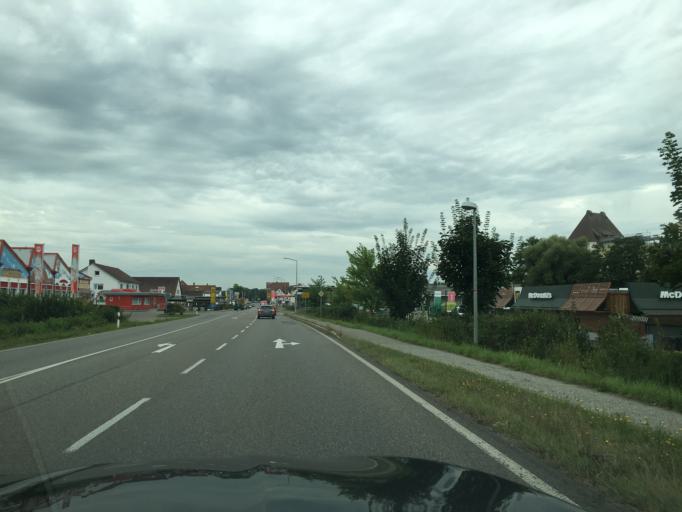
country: DE
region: Baden-Wuerttemberg
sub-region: Tuebingen Region
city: Riedlingen
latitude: 48.1517
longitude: 9.4899
